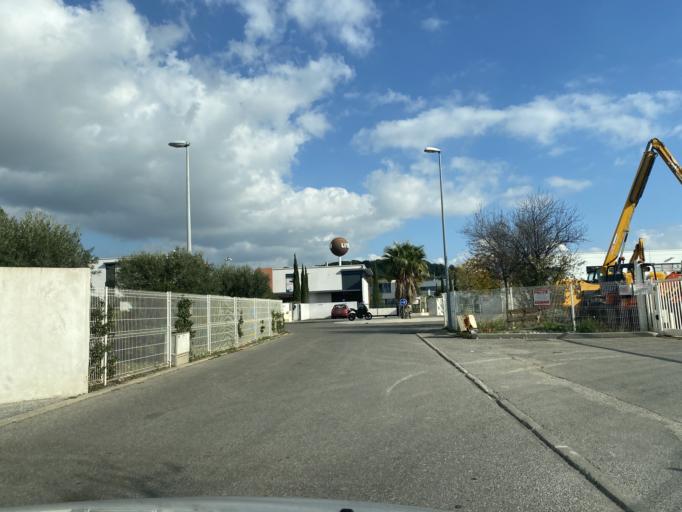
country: FR
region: Provence-Alpes-Cote d'Azur
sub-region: Departement du Var
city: Ollioules
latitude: 43.1225
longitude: 5.8461
